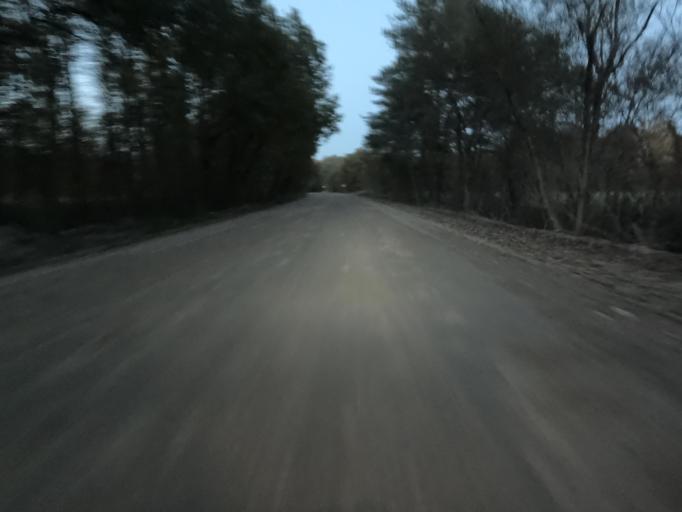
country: RU
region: Leningrad
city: Lyuban'
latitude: 59.1867
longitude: 31.2476
